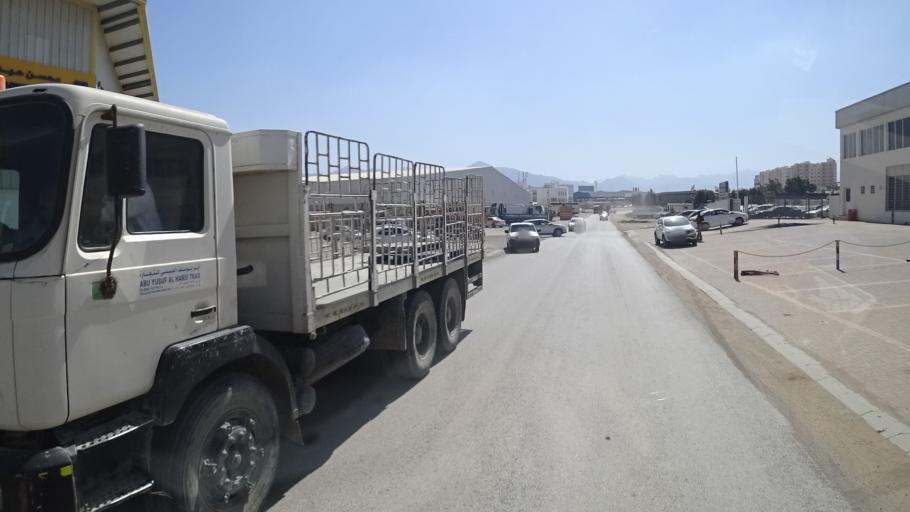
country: OM
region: Muhafazat Masqat
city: Bawshar
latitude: 23.5807
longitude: 58.3688
